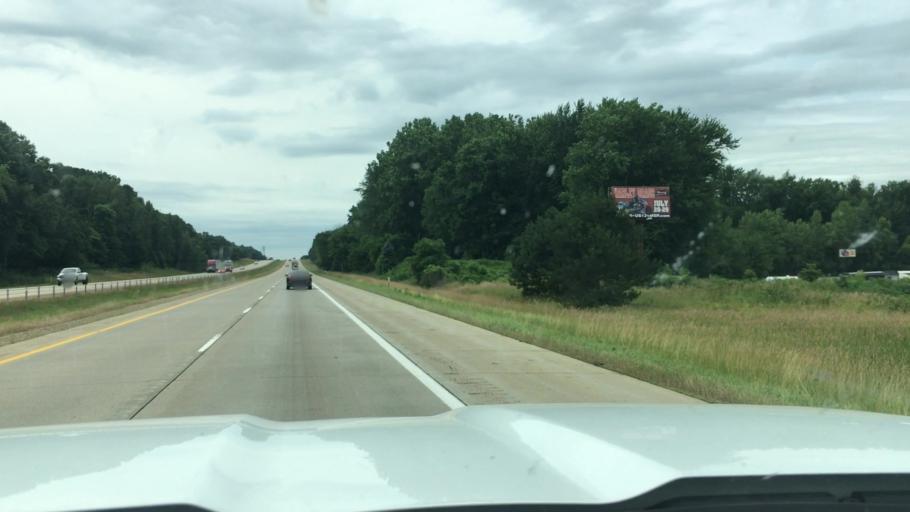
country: US
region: Michigan
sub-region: Allegan County
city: Otsego
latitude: 42.5141
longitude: -85.6557
